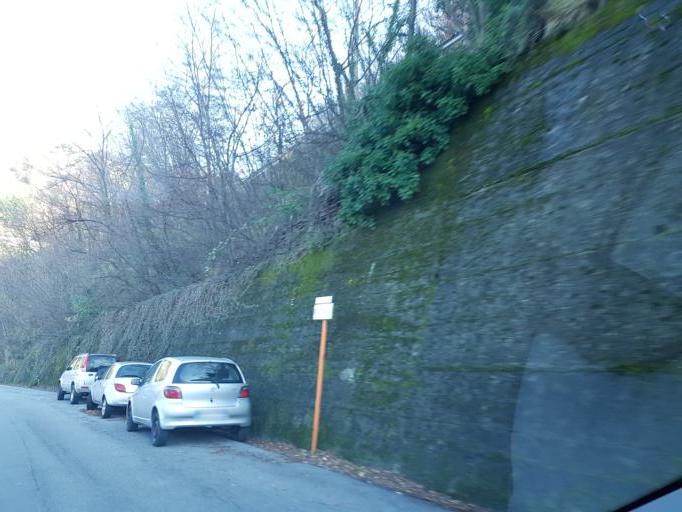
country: IT
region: Liguria
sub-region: Provincia di Genova
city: Manesseno
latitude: 44.4572
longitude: 8.9211
